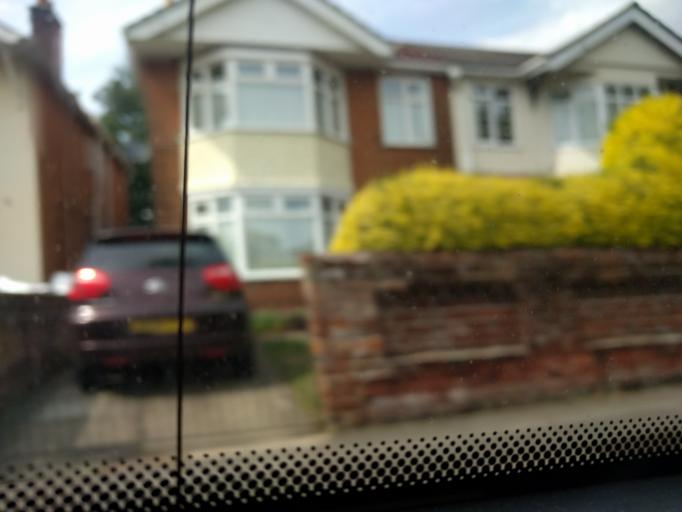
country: GB
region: England
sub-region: Southampton
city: Southampton
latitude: 50.9274
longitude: -1.4327
